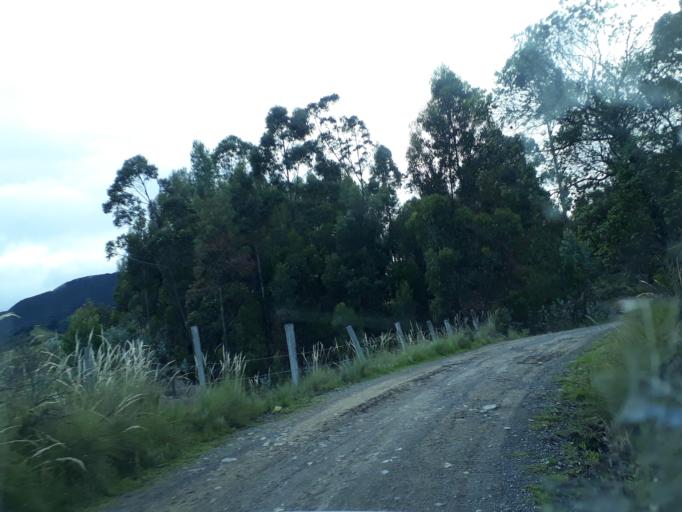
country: CO
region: Cundinamarca
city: Carmen de Carupa
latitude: 5.3154
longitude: -73.9104
